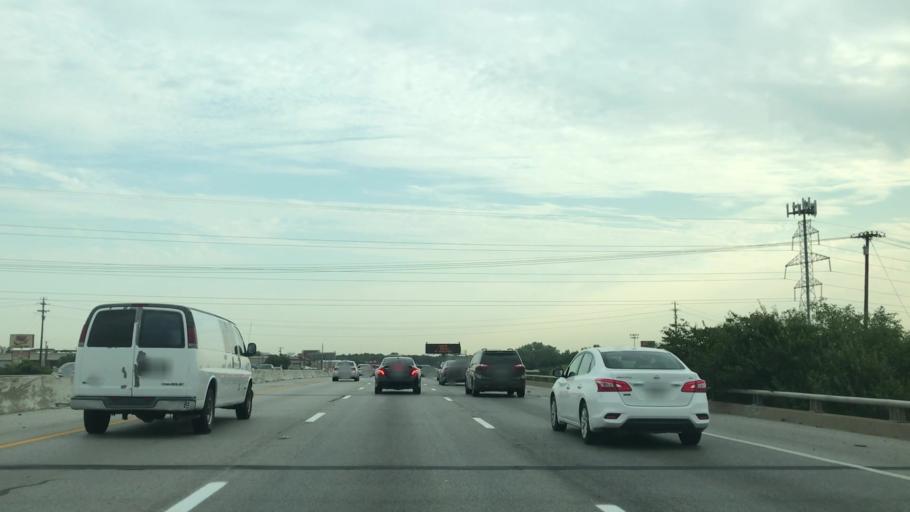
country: US
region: Texas
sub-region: Dallas County
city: Irving
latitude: 32.8142
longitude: -96.9216
